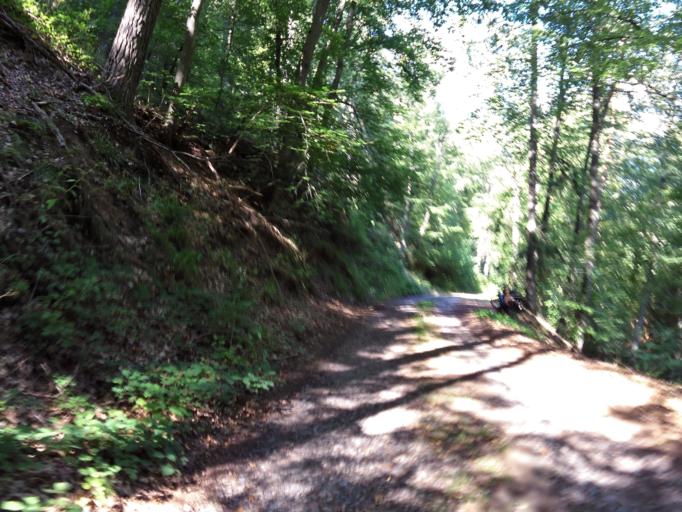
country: DE
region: Rheinland-Pfalz
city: Neidenfels
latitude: 49.4367
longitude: 8.0477
